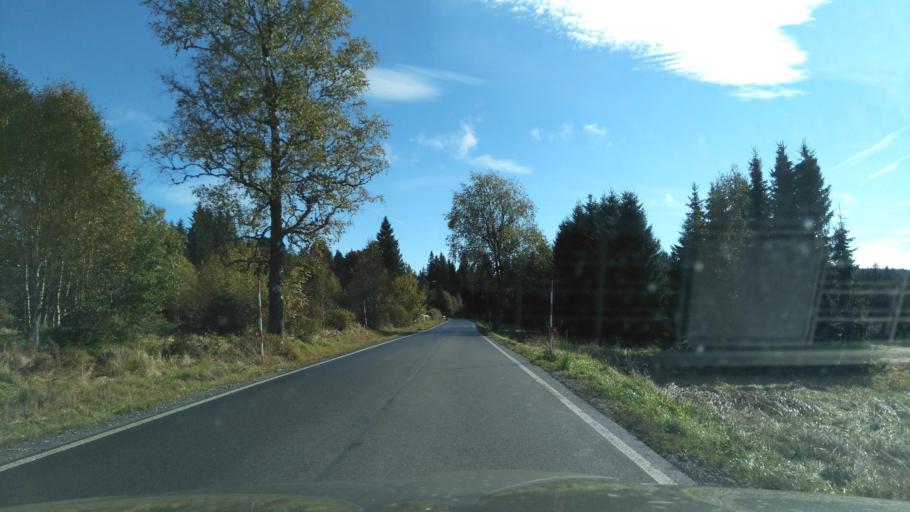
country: CZ
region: Plzensky
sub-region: Okres Klatovy
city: Kasperske Hory
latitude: 49.0298
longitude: 13.5242
